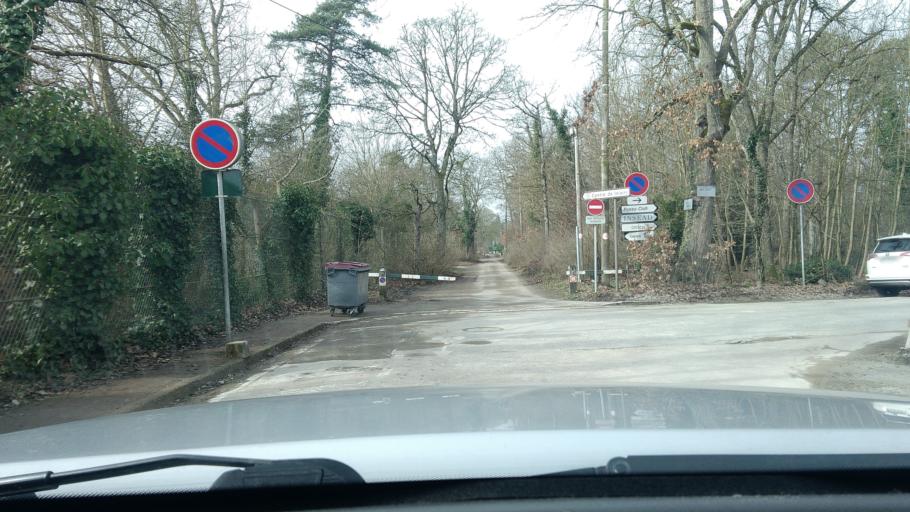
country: FR
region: Ile-de-France
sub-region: Departement de Seine-et-Marne
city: Fontainebleau
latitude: 48.4046
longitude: 2.6829
